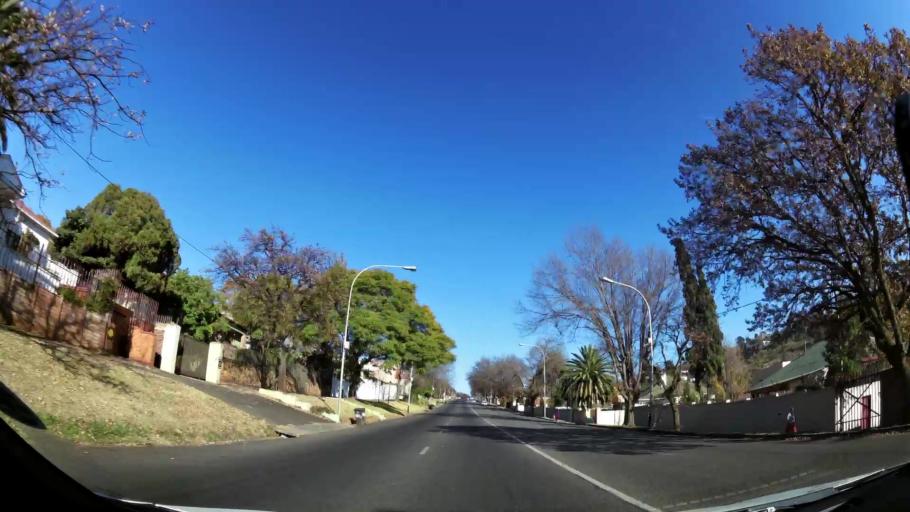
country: ZA
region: Gauteng
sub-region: City of Johannesburg Metropolitan Municipality
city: Johannesburg
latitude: -26.1983
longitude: 28.0868
